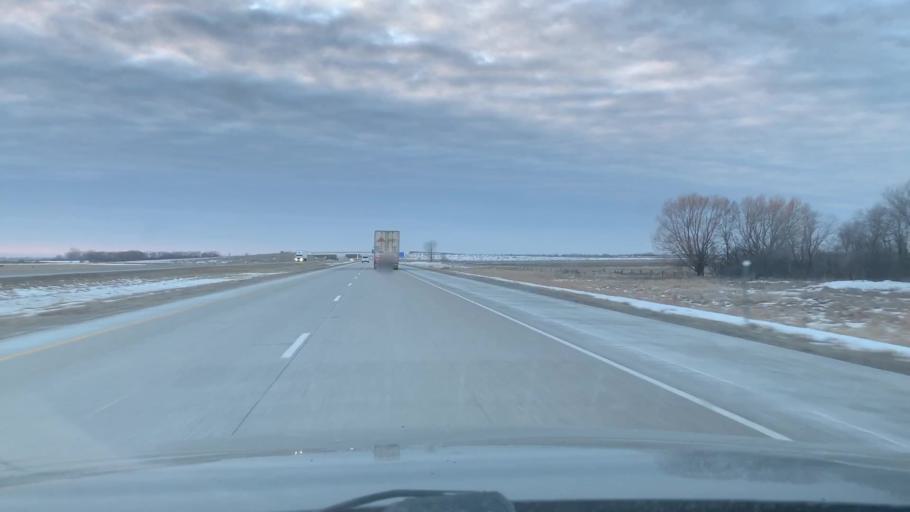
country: US
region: North Dakota
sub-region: Barnes County
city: Valley City
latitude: 46.9196
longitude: -97.7193
